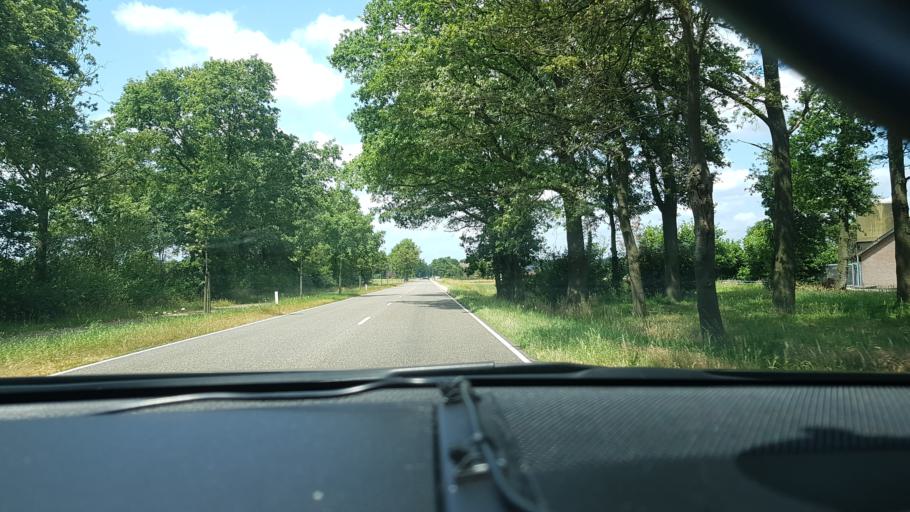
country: NL
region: Limburg
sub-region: Gemeente Leudal
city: Kelpen-Oler
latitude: 51.2504
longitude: 5.8079
